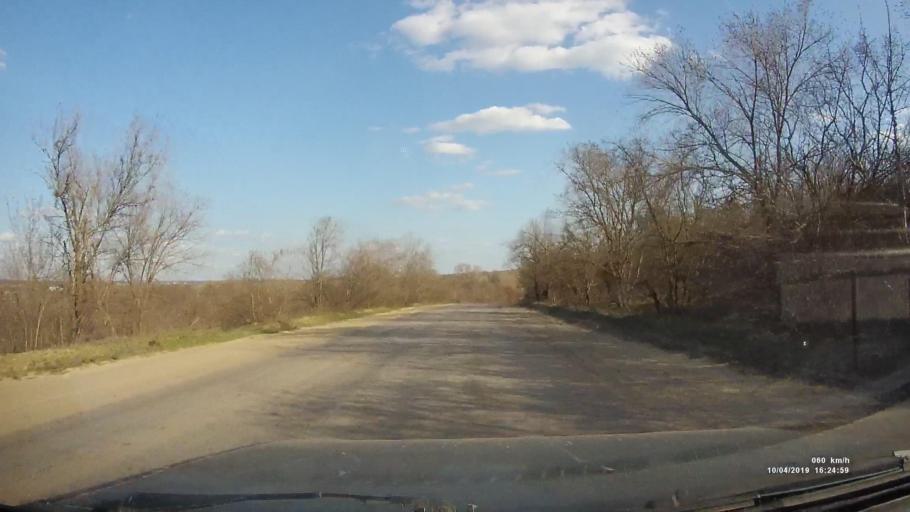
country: RU
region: Rostov
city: Staraya Stanitsa
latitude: 48.2958
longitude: 40.3192
